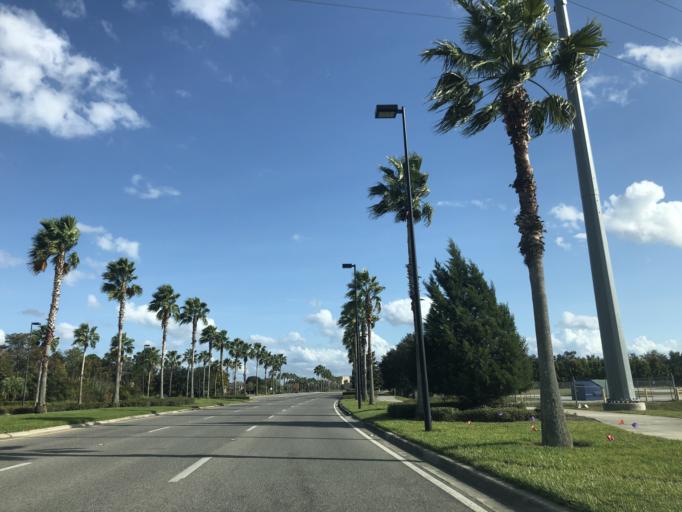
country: US
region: Florida
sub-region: Orange County
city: Williamsburg
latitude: 28.4327
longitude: -81.4540
